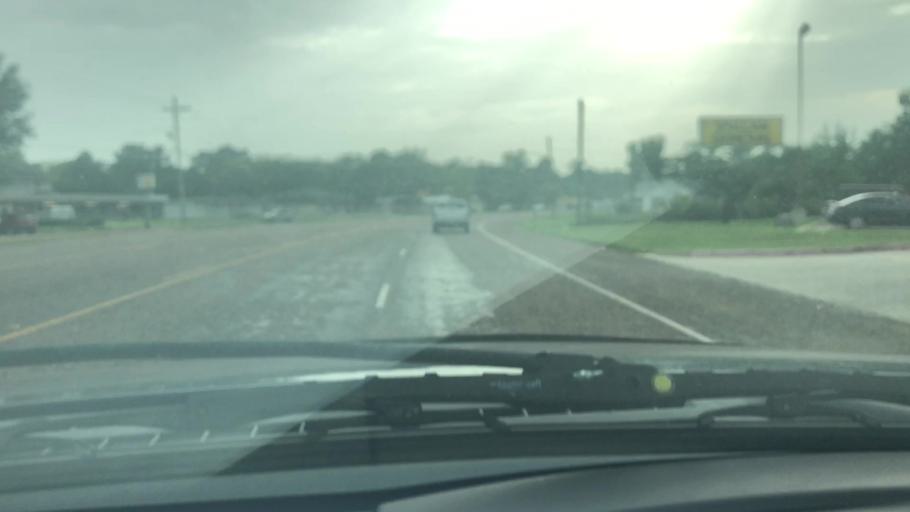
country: US
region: Texas
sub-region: Bowie County
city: Texarkana
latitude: 33.4009
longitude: -94.0685
